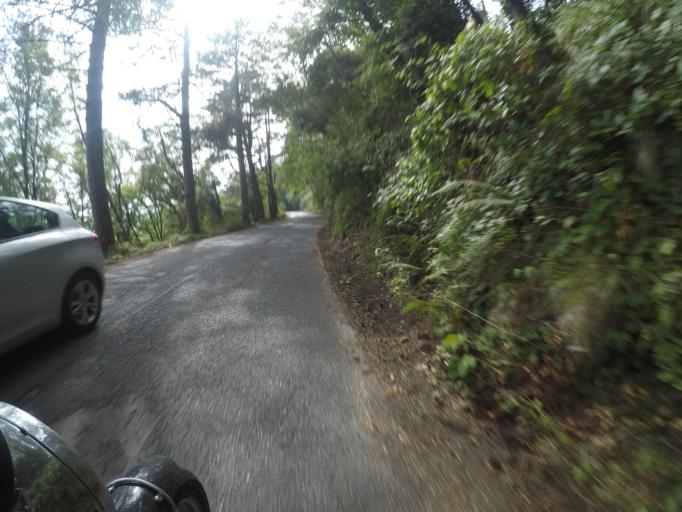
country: IT
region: Tuscany
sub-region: Provincia di Massa-Carrara
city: Fosdinovo
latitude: 44.1218
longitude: 10.0776
